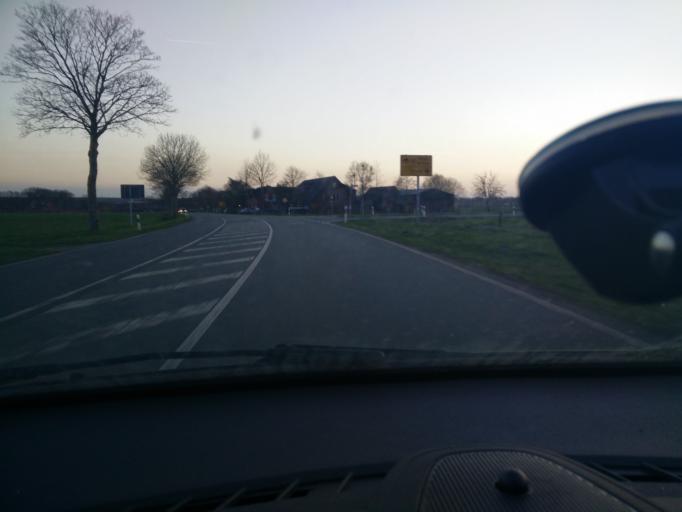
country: DE
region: North Rhine-Westphalia
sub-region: Regierungsbezirk Munster
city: Rhede
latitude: 51.7426
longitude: 6.7311
